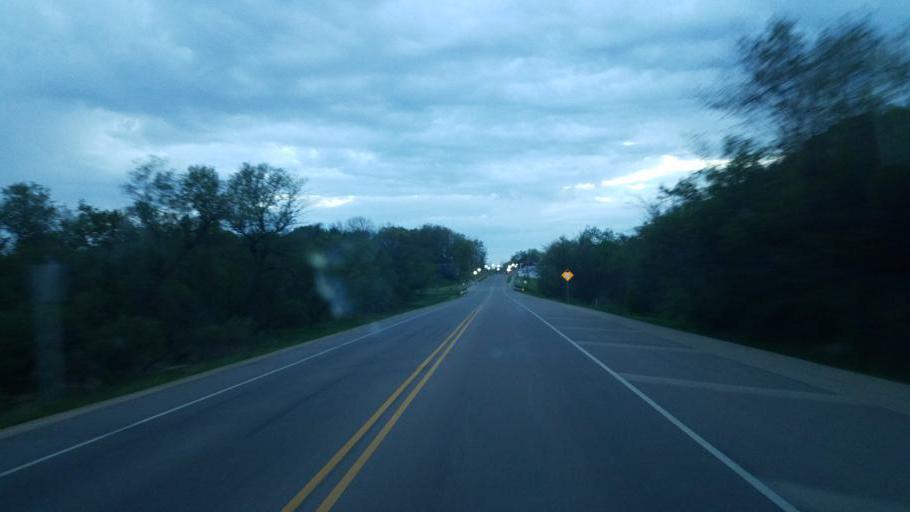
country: US
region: Wisconsin
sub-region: Juneau County
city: Elroy
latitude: 43.7315
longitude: -90.2672
